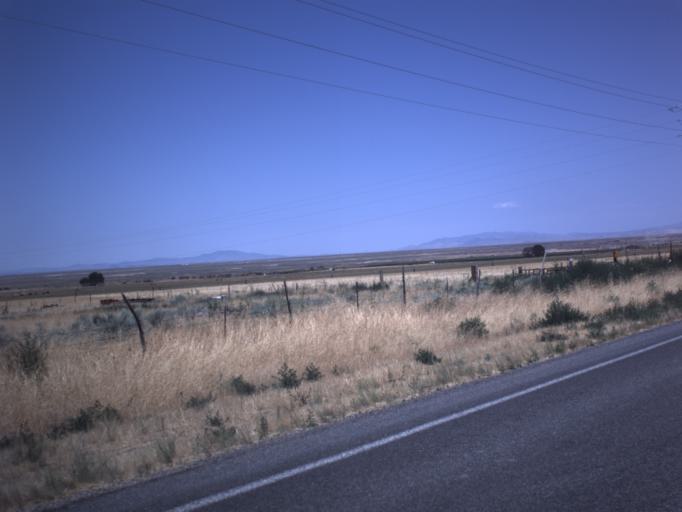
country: US
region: Utah
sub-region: Millard County
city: Delta
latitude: 39.3950
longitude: -112.3354
